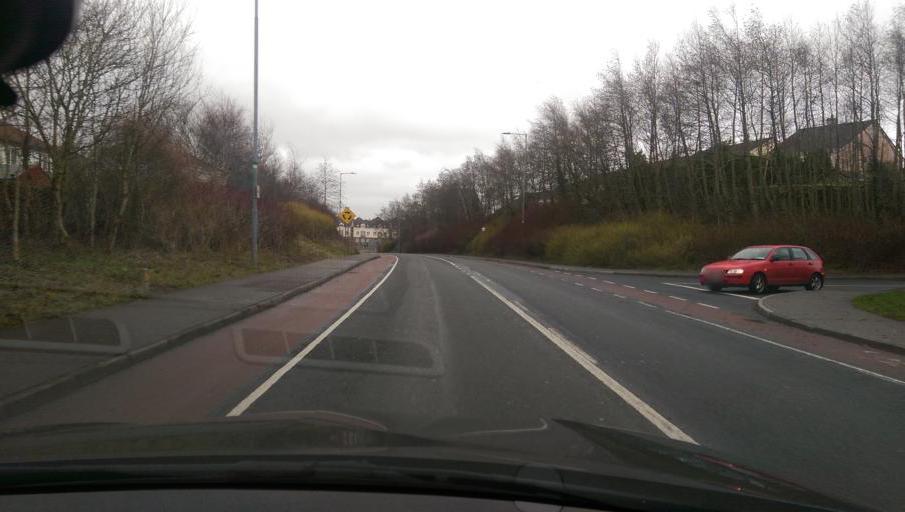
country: IE
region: Connaught
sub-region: County Galway
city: Gaillimh
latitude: 53.2704
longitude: -9.0910
